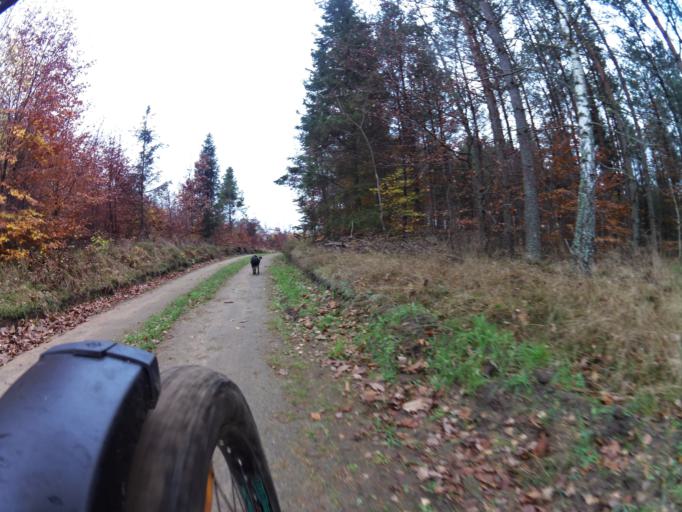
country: PL
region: Pomeranian Voivodeship
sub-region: Powiat wejherowski
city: Orle
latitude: 54.7003
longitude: 18.1550
